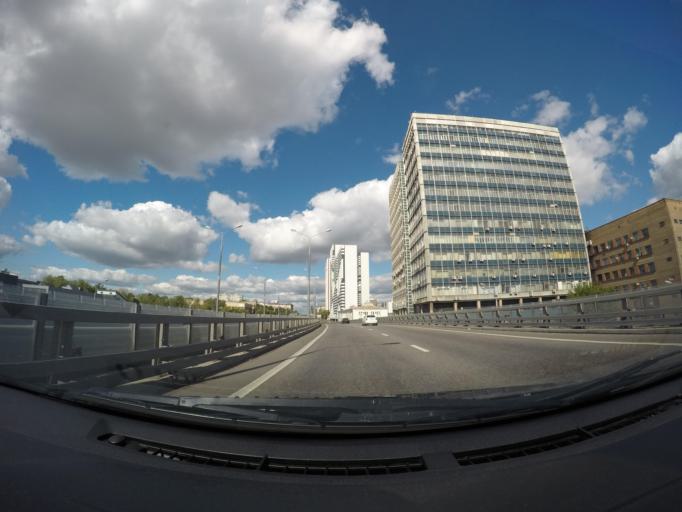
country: RU
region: Moscow
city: Ryazanskiy
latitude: 55.7563
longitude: 37.7408
